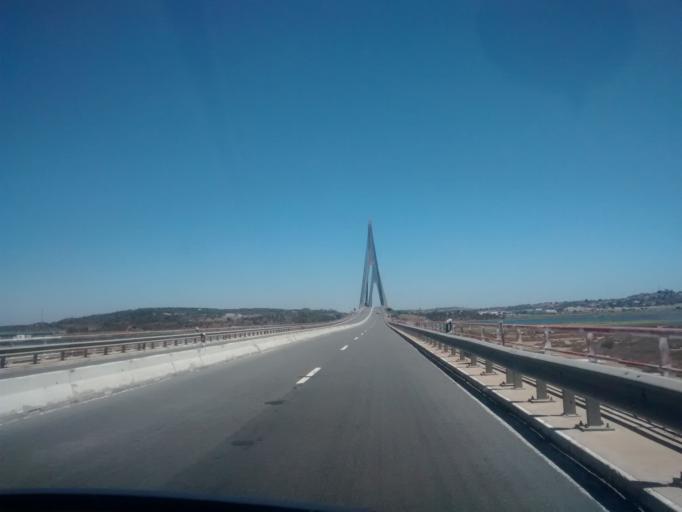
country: PT
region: Faro
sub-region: Castro Marim
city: Castro Marim
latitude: 37.2376
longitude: -7.4283
